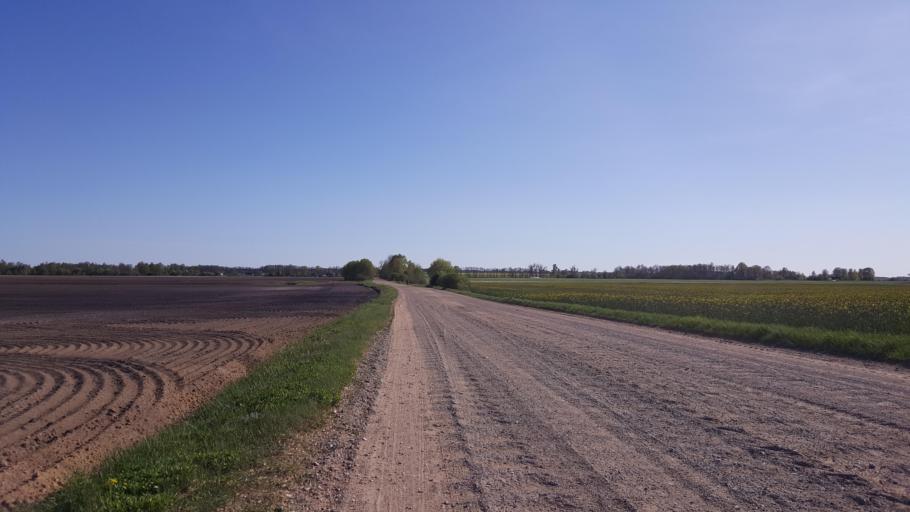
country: BY
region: Brest
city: Kamyanyets
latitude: 52.4320
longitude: 23.8838
